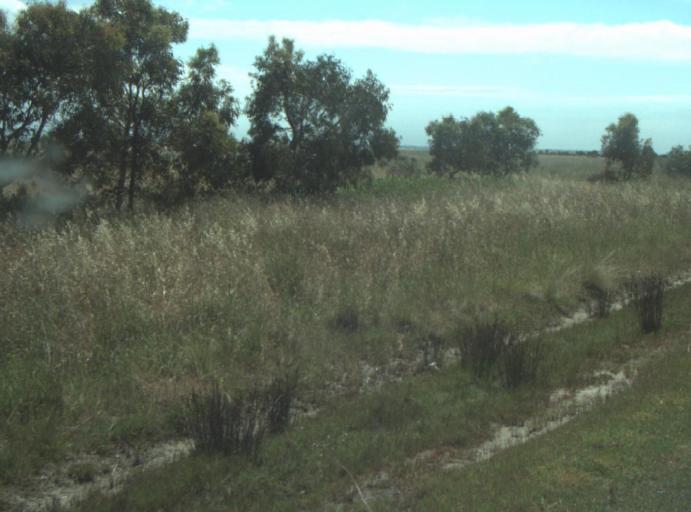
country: AU
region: Victoria
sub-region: Greater Geelong
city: Leopold
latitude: -38.2680
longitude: 144.4434
